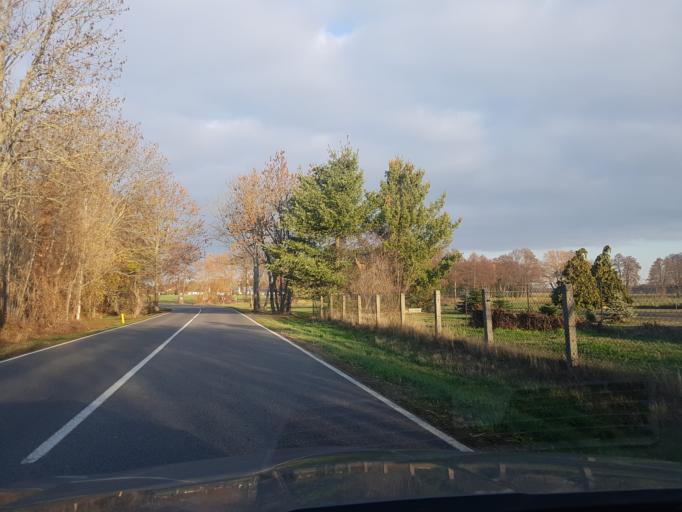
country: DE
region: Brandenburg
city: Luckau
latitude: 51.8733
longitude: 13.6982
